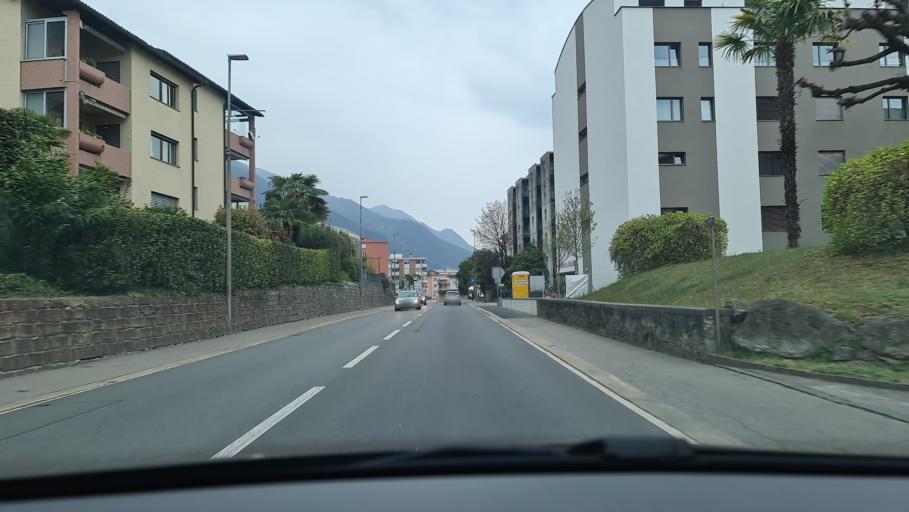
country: CH
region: Ticino
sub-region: Locarno District
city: Minusio
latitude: 46.1786
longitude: 8.8230
